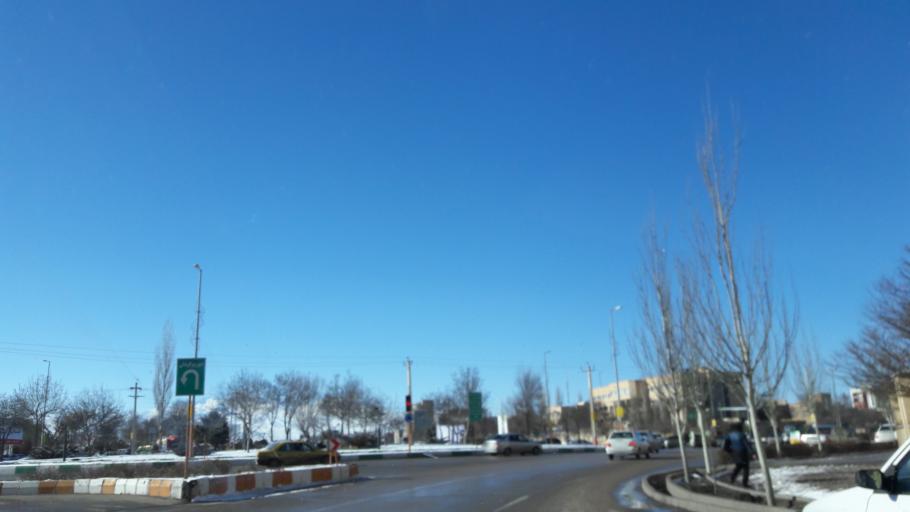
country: IR
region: Ardabil
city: Ardabil
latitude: 38.2189
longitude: 48.2962
